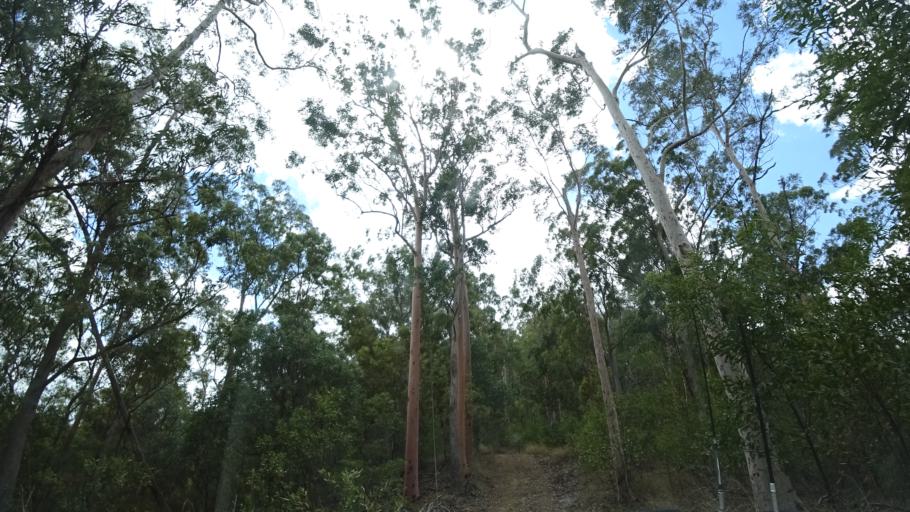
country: AU
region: Queensland
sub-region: Moreton Bay
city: Highvale
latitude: -27.4088
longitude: 152.7401
